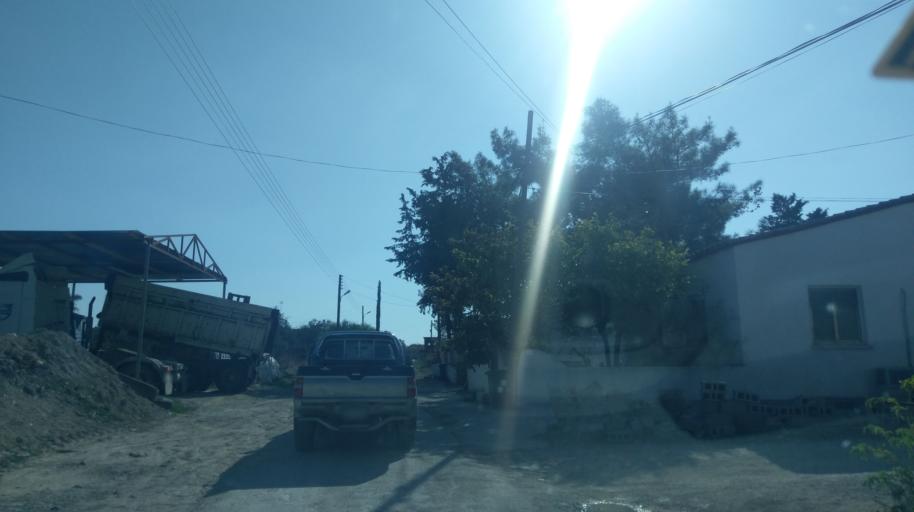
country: CY
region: Lefkosia
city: Lympia
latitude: 35.0072
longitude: 33.4643
